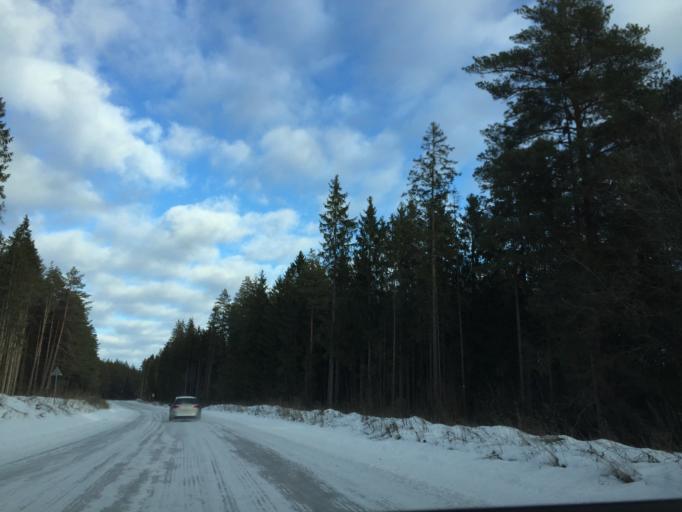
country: LV
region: Ogre
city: Jumprava
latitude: 56.5712
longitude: 24.9354
